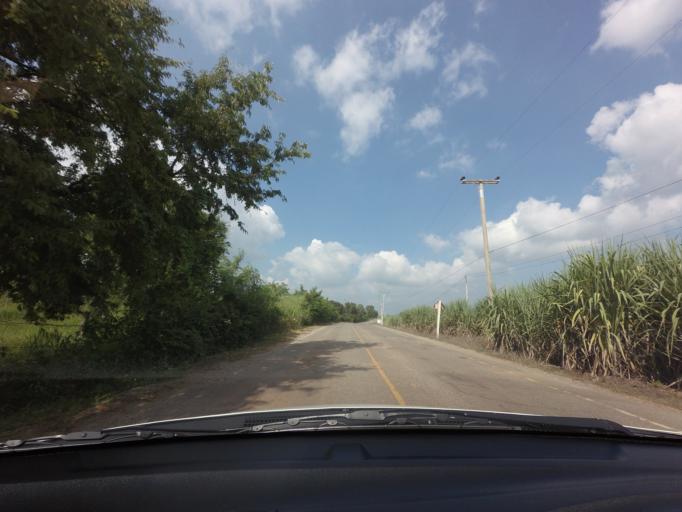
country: TH
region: Nakhon Ratchasima
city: Wang Nam Khiao
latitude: 14.5325
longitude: 101.6304
